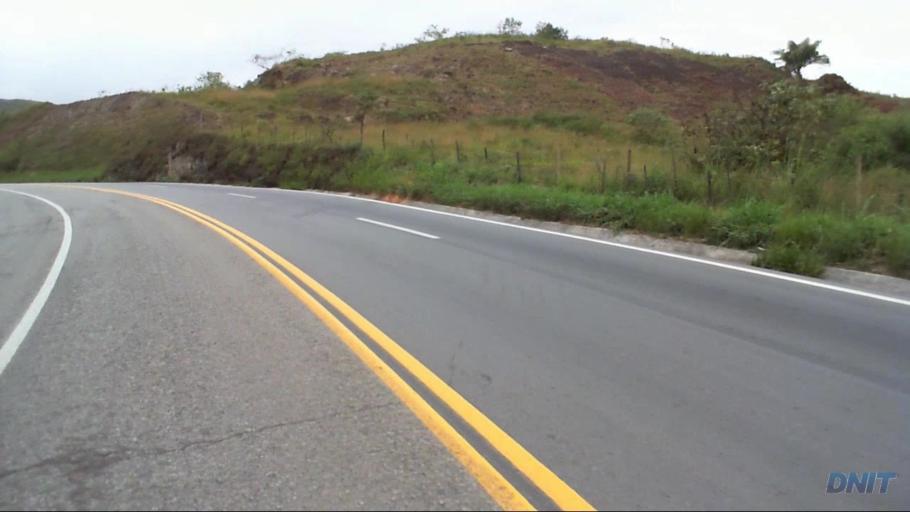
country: BR
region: Minas Gerais
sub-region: Nova Era
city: Nova Era
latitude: -19.6888
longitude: -42.9905
